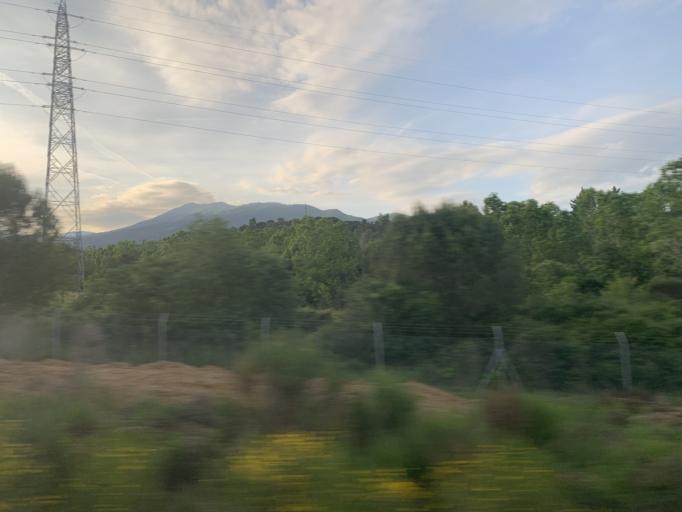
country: ES
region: Catalonia
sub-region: Provincia de Barcelona
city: Sant Celoni
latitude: 41.6954
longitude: 2.4853
